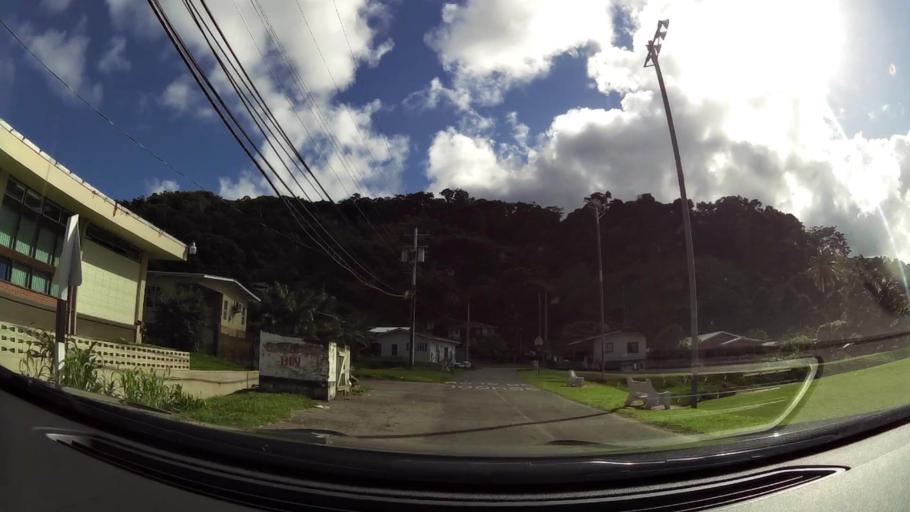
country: TT
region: Eastern Tobago
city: Roxborough
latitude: 11.3228
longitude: -60.5475
